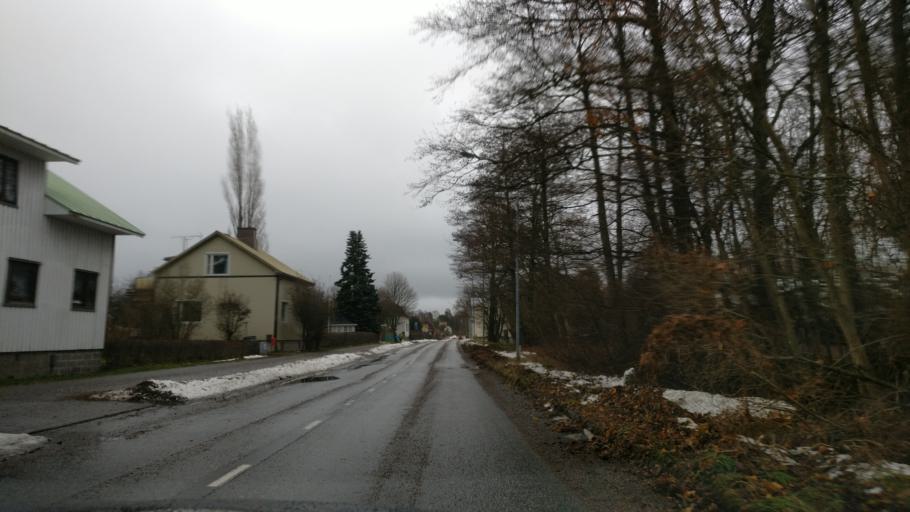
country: FI
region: Uusimaa
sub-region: Raaseporin
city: Hanko
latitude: 59.8329
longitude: 22.9386
